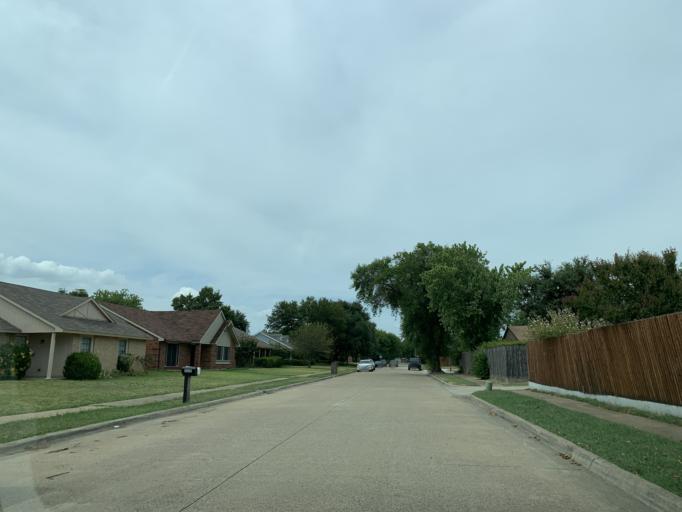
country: US
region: Texas
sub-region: Dallas County
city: Cedar Hill
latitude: 32.6517
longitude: -97.0345
